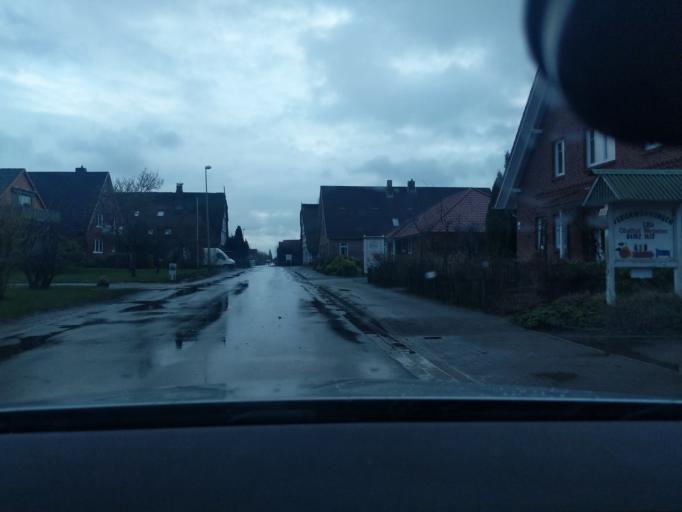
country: DE
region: Lower Saxony
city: Jork
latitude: 53.5208
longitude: 9.6614
